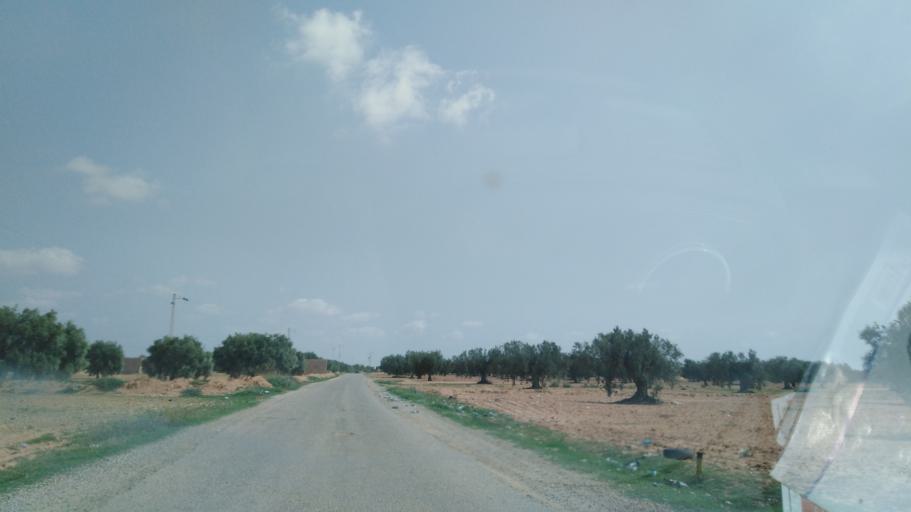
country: TN
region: Safaqis
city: Sfax
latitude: 34.6340
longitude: 10.6059
